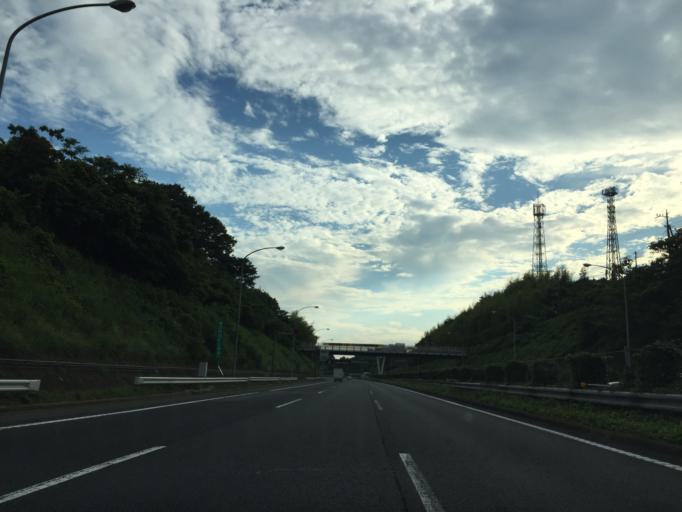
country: JP
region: Tokyo
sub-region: Machida-shi
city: Machida
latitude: 35.5153
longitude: 139.4940
